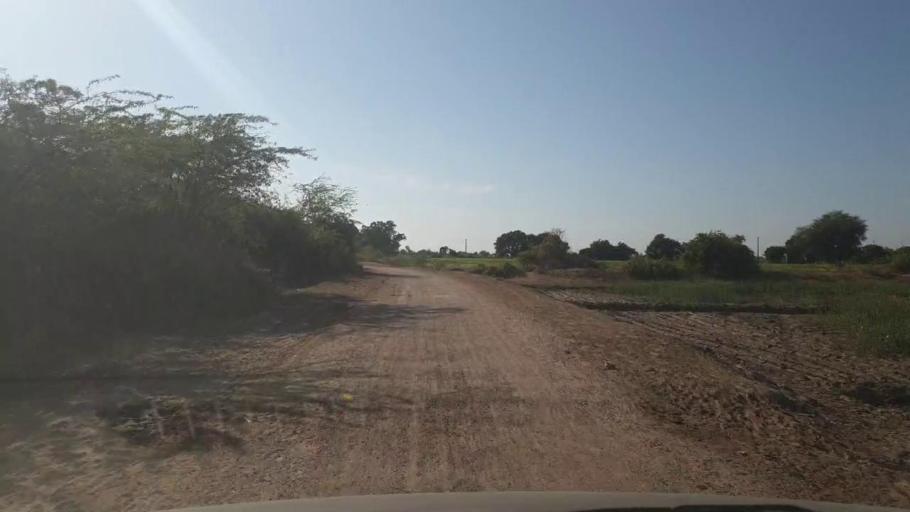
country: PK
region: Sindh
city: Dhoro Naro
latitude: 25.4127
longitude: 69.5702
